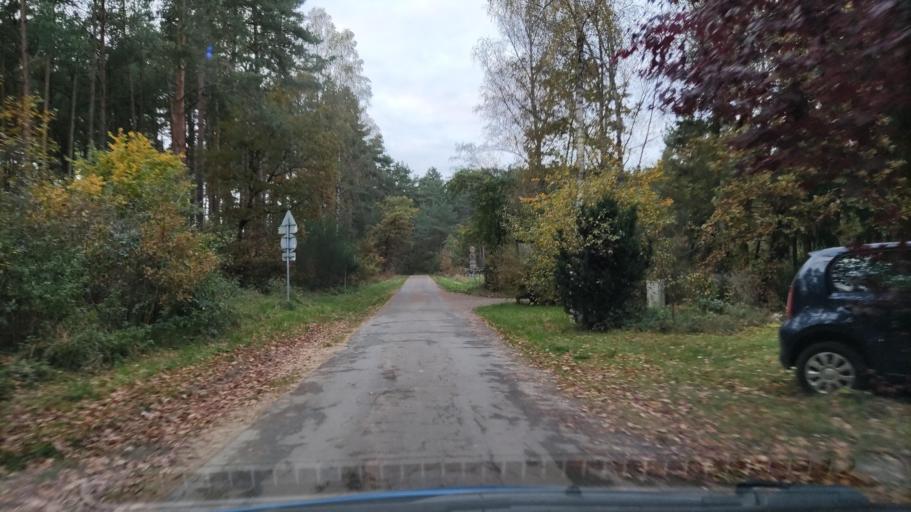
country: DE
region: Lower Saxony
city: Karwitz
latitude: 53.1291
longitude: 10.9909
